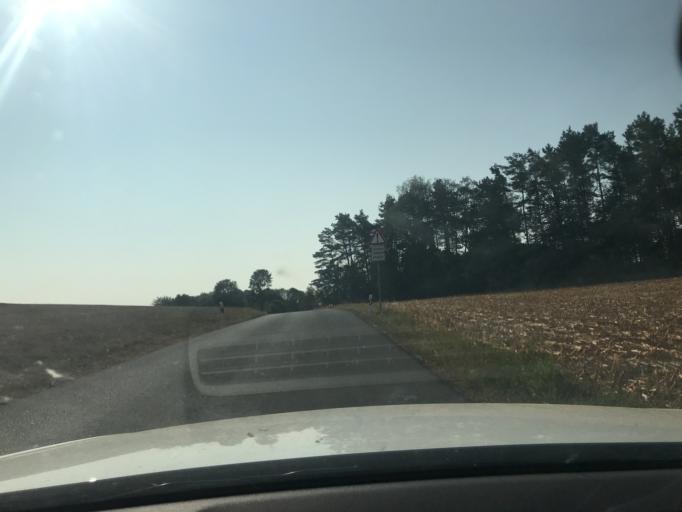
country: DE
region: Bavaria
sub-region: Upper Franconia
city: Pegnitz
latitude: 49.7370
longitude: 11.5762
